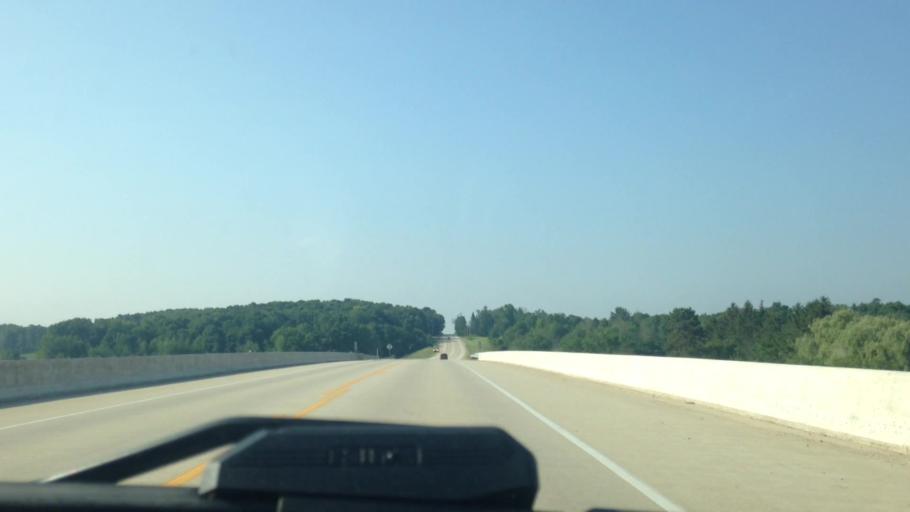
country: US
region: Wisconsin
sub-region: Washington County
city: Slinger
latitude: 43.3105
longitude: -88.2607
